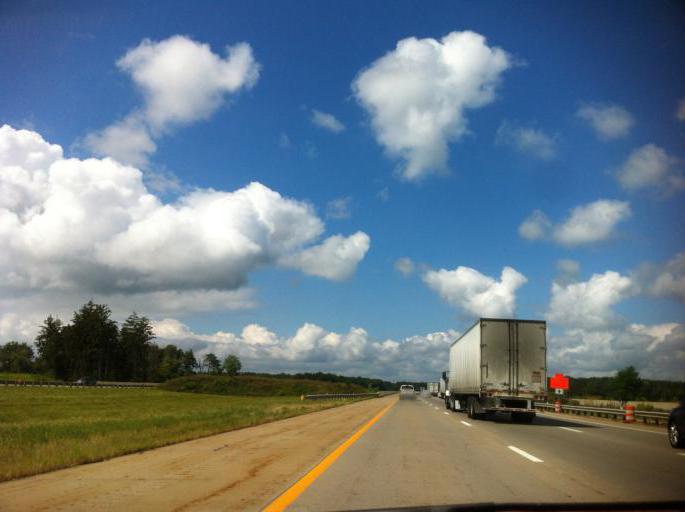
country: US
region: Ohio
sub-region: Mahoning County
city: Austintown
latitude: 41.1159
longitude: -80.8048
